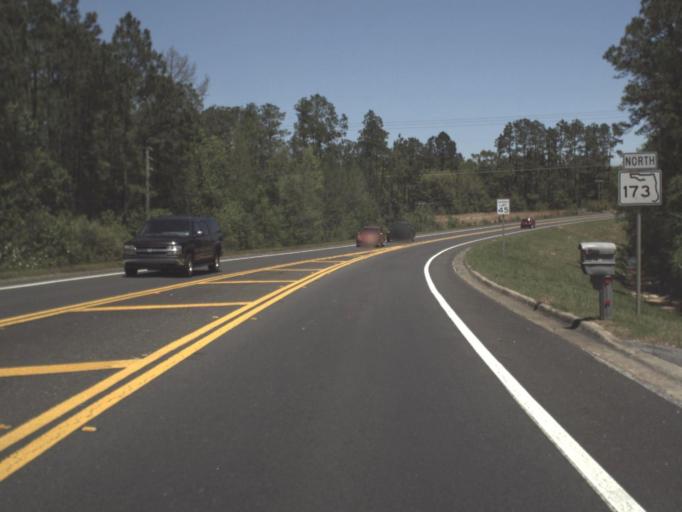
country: US
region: Florida
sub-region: Escambia County
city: Bellview
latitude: 30.4853
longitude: -87.3226
